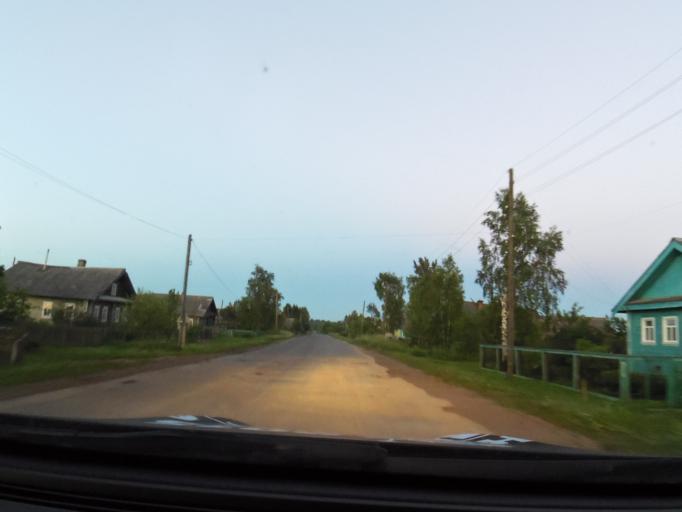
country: RU
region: Vologda
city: Vytegra
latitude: 60.9932
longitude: 36.3461
